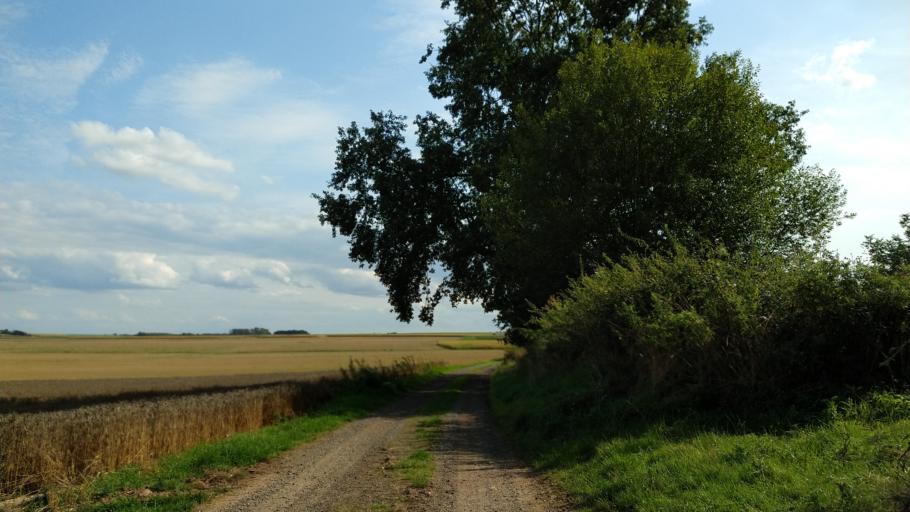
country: BE
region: Flanders
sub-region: Provincie Vlaams-Brabant
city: Boutersem
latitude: 50.8337
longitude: 4.8473
